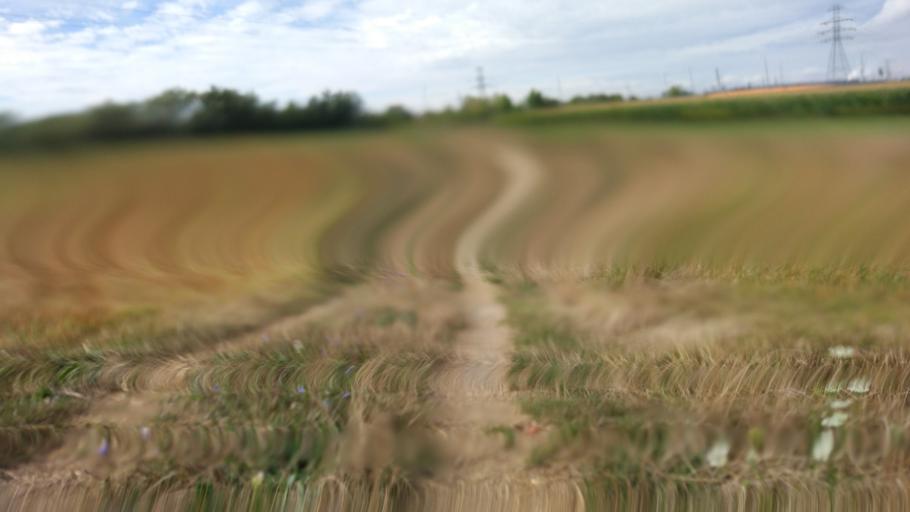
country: PL
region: Masovian Voivodeship
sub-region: Plock
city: Plock
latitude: 52.5300
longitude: 19.7406
